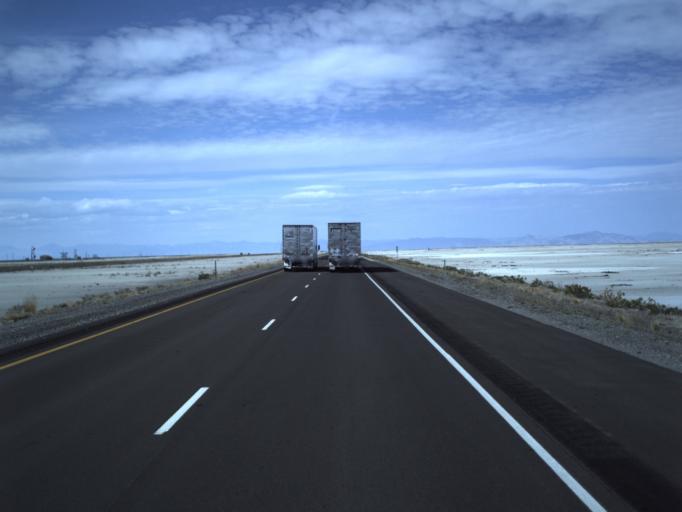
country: US
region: Utah
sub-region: Tooele County
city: Wendover
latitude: 40.7312
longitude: -113.4721
